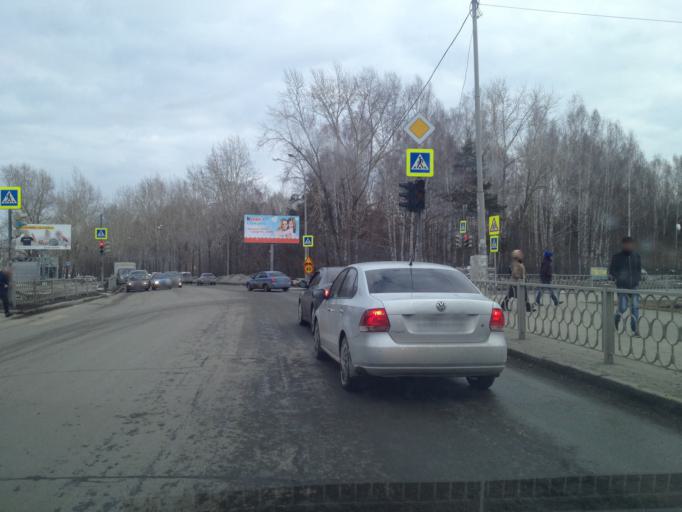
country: RU
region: Sverdlovsk
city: Yekaterinburg
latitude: 56.8667
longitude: 60.5596
